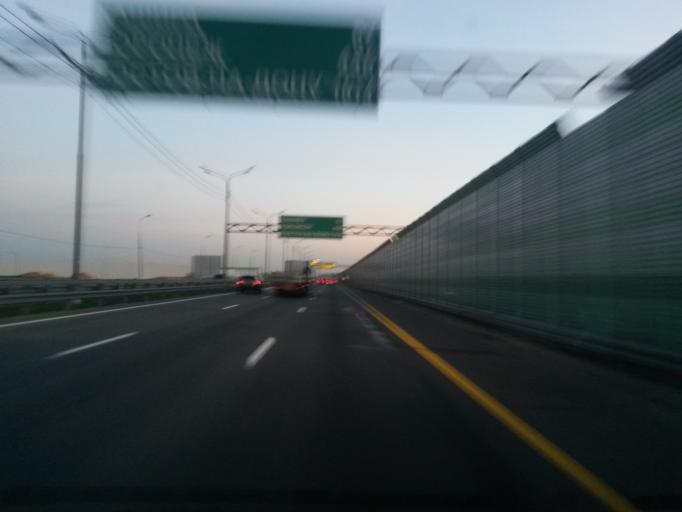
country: RU
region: Moskovskaya
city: Belyye Stolby
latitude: 55.3333
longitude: 37.8093
